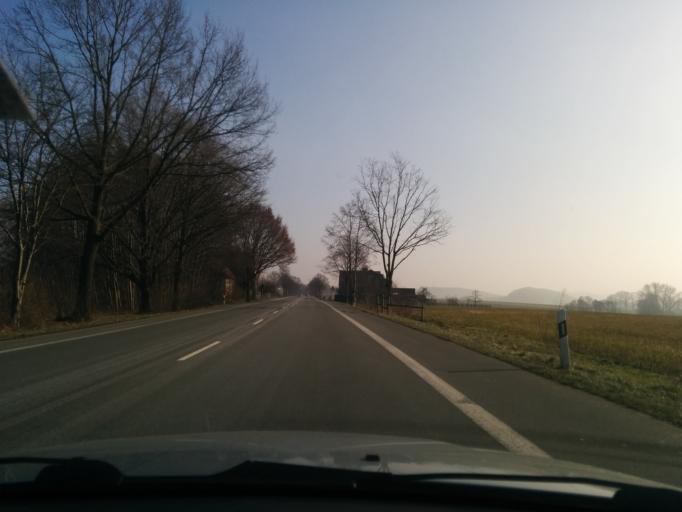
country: DE
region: North Rhine-Westphalia
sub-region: Regierungsbezirk Detmold
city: Dorentrup
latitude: 51.9998
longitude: 8.9735
